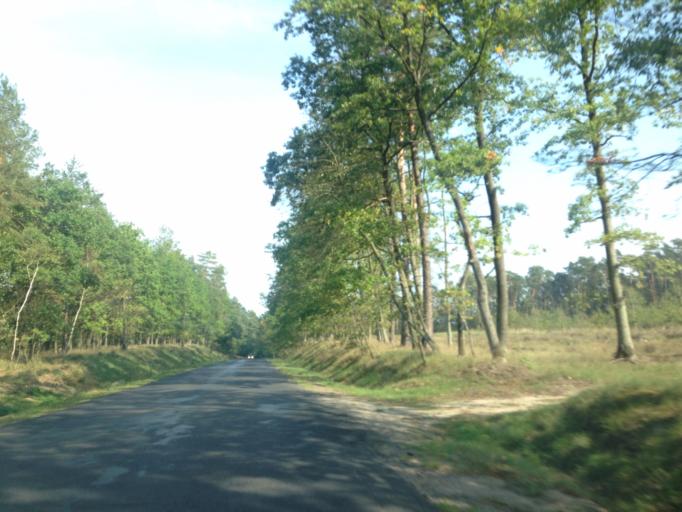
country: PL
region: Kujawsko-Pomorskie
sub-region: Powiat golubsko-dobrzynski
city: Golub-Dobrzyn
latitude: 53.0893
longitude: 18.9886
